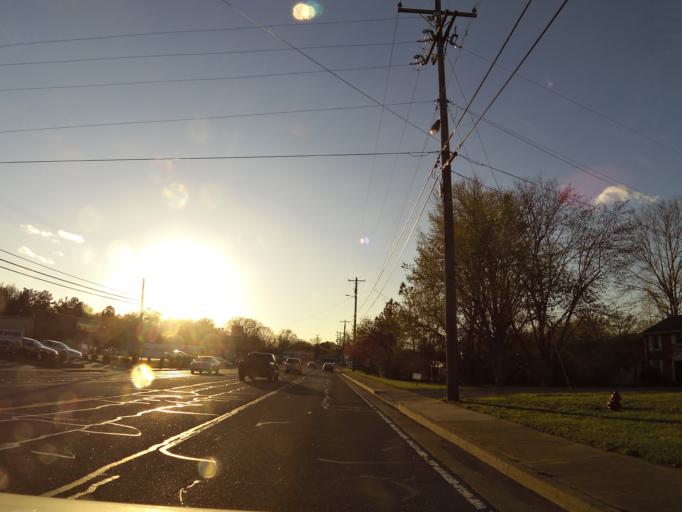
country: US
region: Tennessee
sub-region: Robertson County
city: Ridgetop
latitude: 36.3965
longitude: -86.7672
